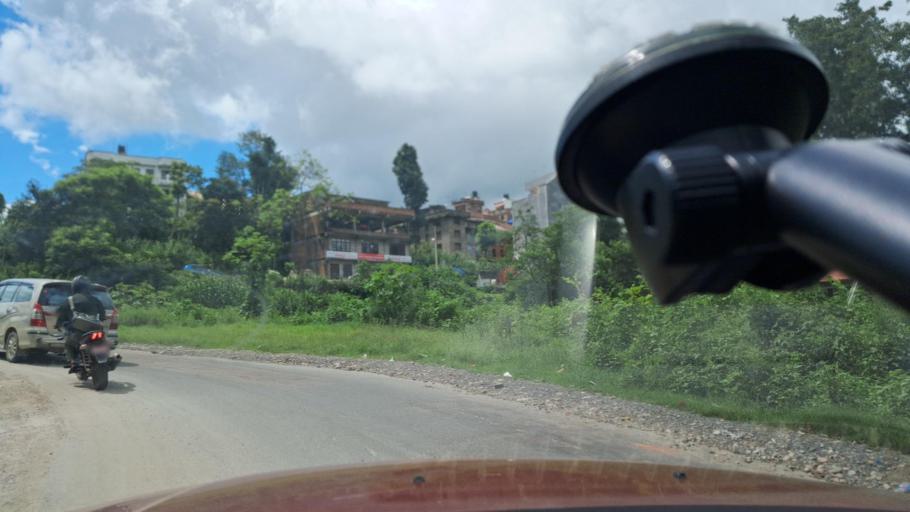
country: NP
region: Central Region
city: Banepa
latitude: 27.6166
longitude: 85.5517
